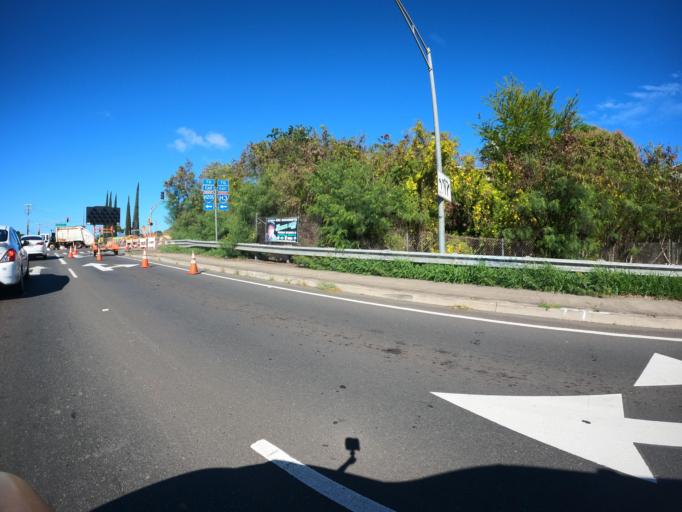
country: US
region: Hawaii
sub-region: Honolulu County
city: Halawa
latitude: 21.3732
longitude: -157.9192
